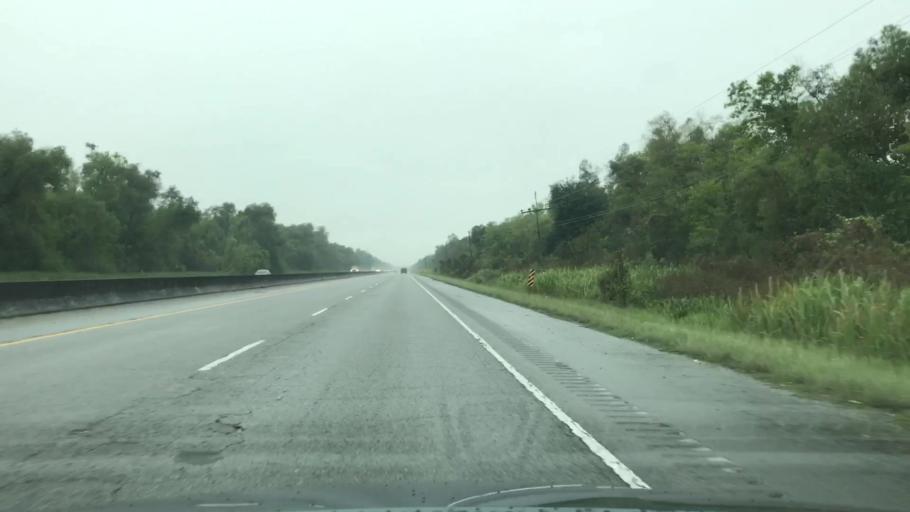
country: US
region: Louisiana
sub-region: Saint Charles Parish
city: Des Allemands
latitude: 29.7773
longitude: -90.5303
